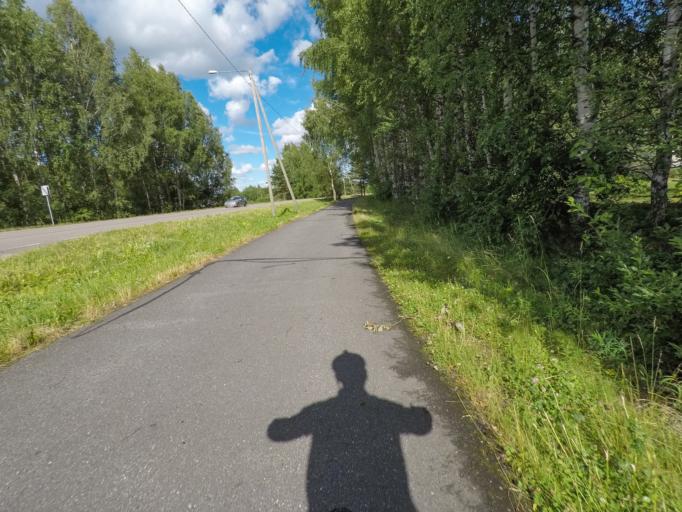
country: FI
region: South Karelia
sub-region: Lappeenranta
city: Joutseno
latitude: 61.1279
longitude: 28.4988
